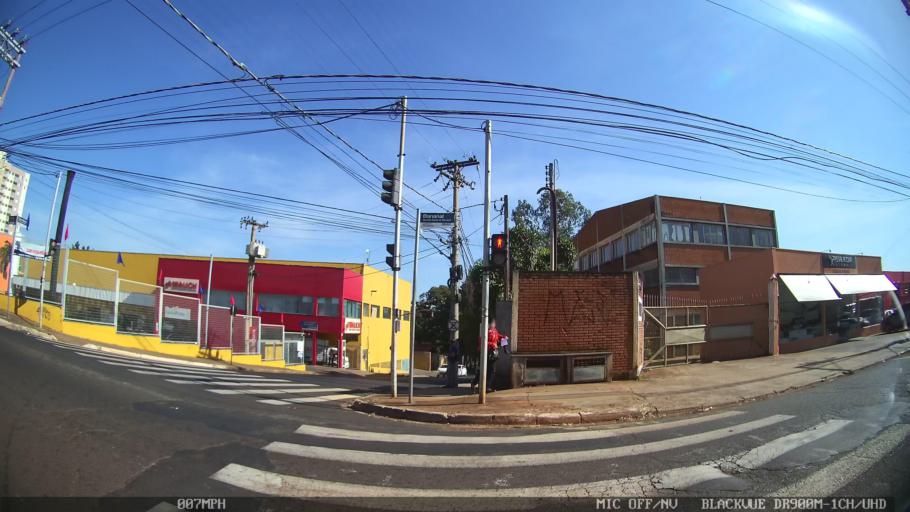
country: BR
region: Sao Paulo
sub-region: Ribeirao Preto
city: Ribeirao Preto
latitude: -21.1814
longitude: -47.7749
